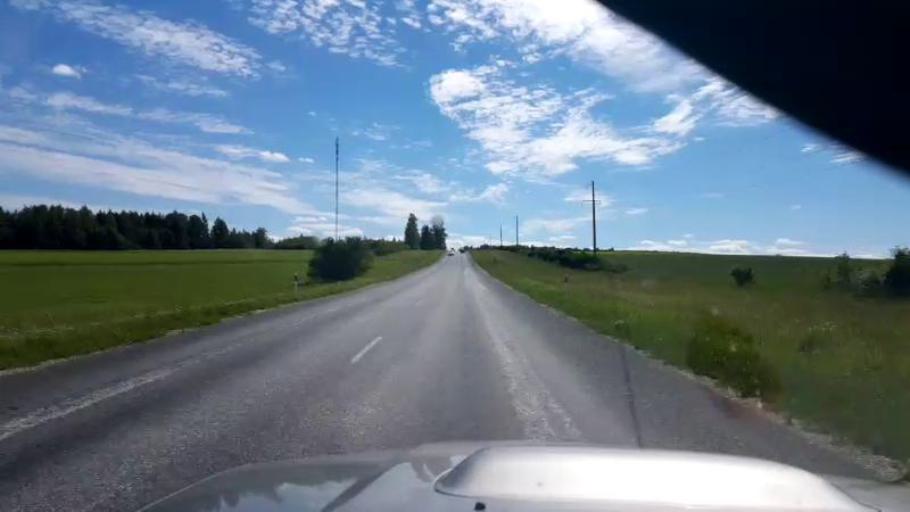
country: EE
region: Laeaene-Virumaa
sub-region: Rakke vald
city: Rakke
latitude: 58.8537
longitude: 26.2920
